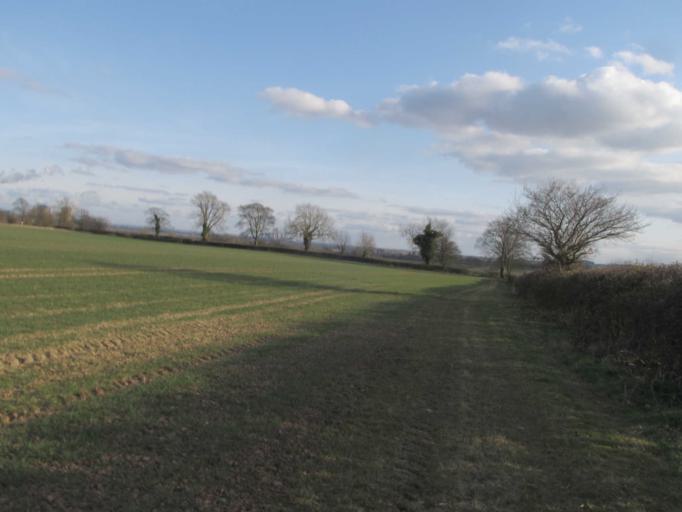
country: GB
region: England
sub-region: Nottinghamshire
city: Misterton
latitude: 53.3793
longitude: -0.8631
